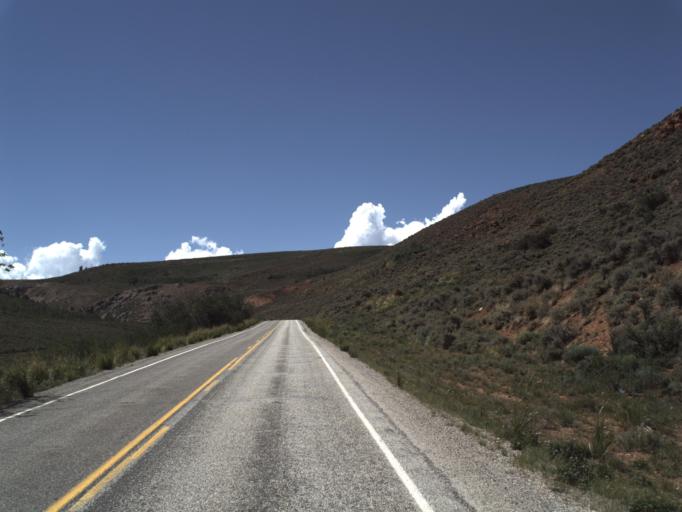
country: US
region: Utah
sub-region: Rich County
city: Randolph
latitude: 41.4779
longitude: -111.3646
